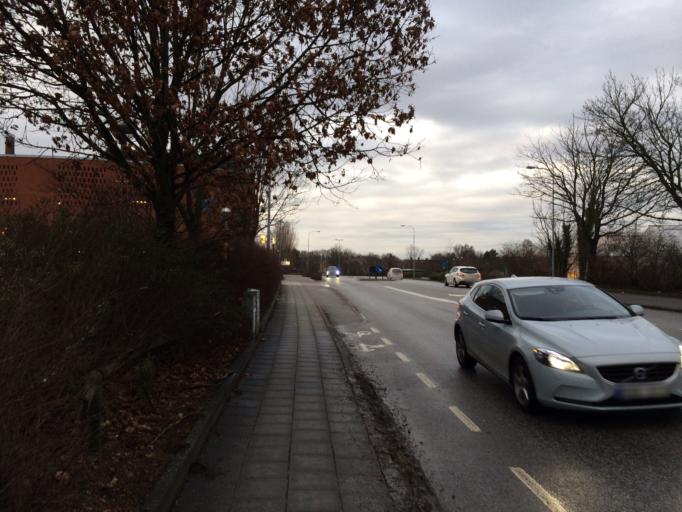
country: SE
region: Skane
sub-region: Lunds Kommun
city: Lund
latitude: 55.7119
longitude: 13.2053
